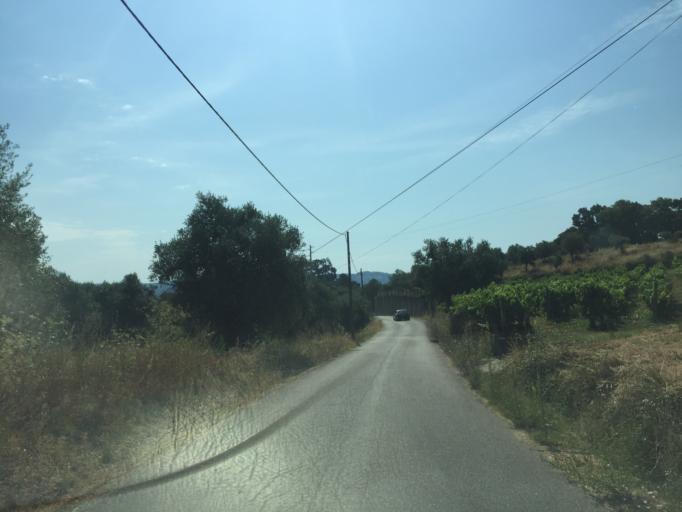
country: PT
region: Santarem
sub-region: Ferreira do Zezere
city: Ferreira do Zezere
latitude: 39.6069
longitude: -8.2857
